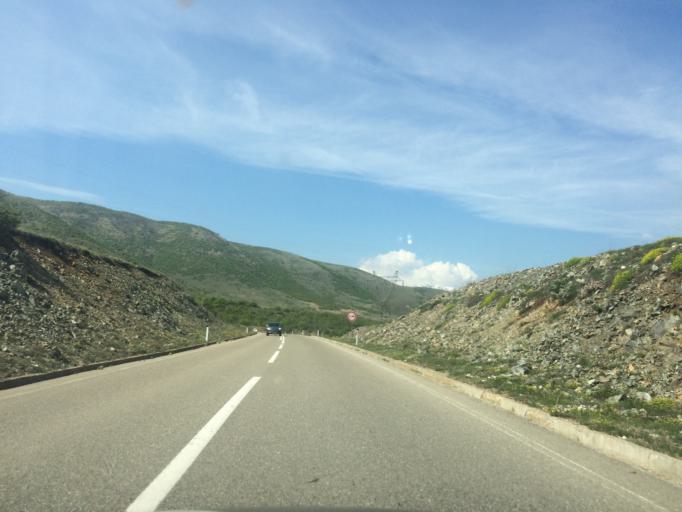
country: XK
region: Gjakova
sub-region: Komuna e Junikut
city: Junik
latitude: 42.4044
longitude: 20.2465
